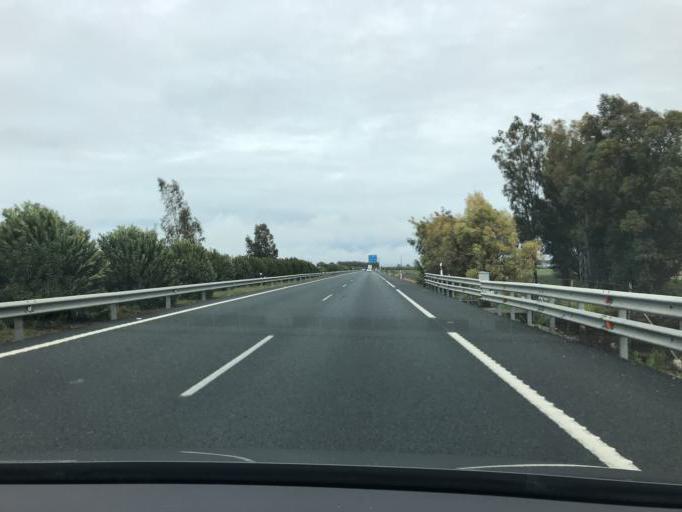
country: ES
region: Andalusia
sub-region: Provincia de Sevilla
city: El Arahal
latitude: 37.2554
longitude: -5.5931
